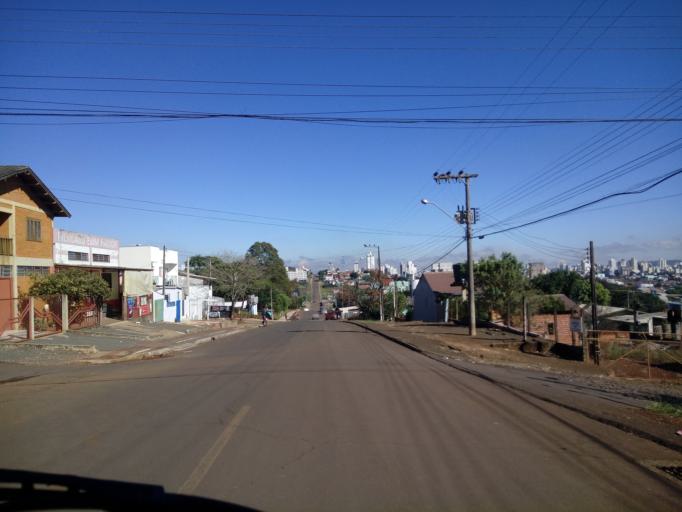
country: BR
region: Santa Catarina
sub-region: Chapeco
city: Chapeco
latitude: -27.0998
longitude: -52.5919
